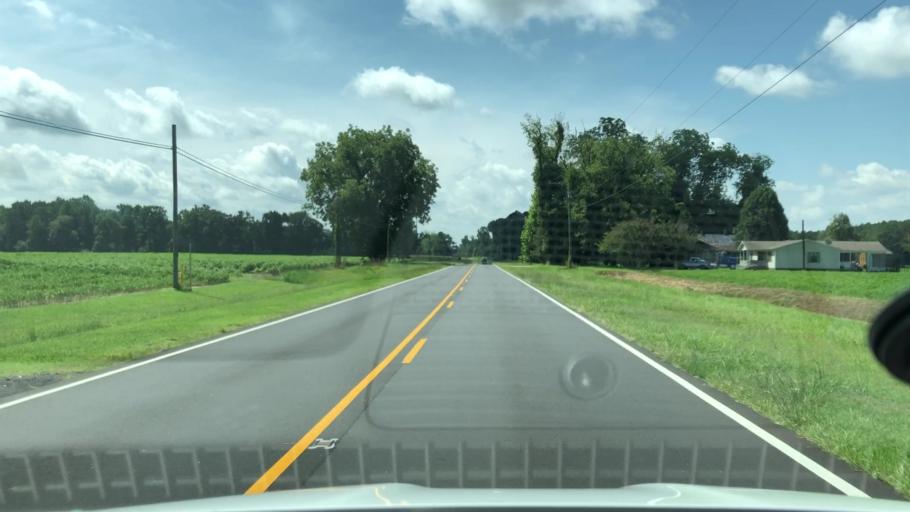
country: US
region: North Carolina
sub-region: Martin County
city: Williamston
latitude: 35.7623
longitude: -77.0747
